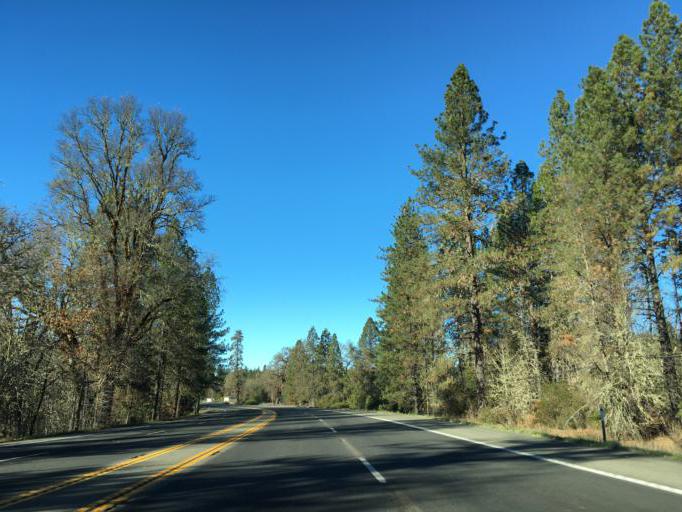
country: US
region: California
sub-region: Mendocino County
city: Laytonville
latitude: 39.7259
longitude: -123.5039
